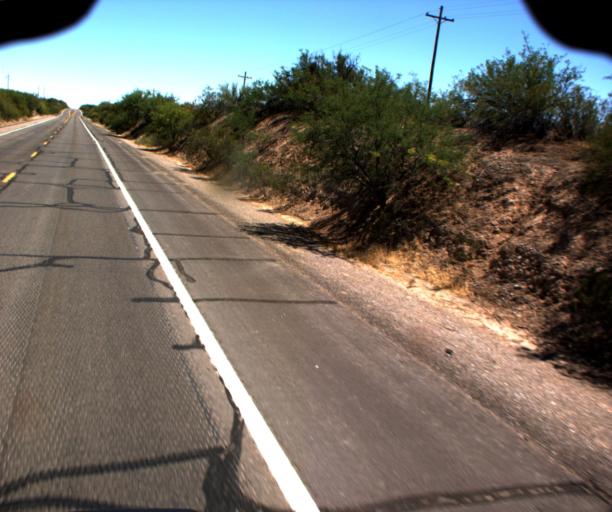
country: US
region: Arizona
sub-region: Pinal County
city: Mammoth
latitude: 32.7951
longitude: -110.6757
